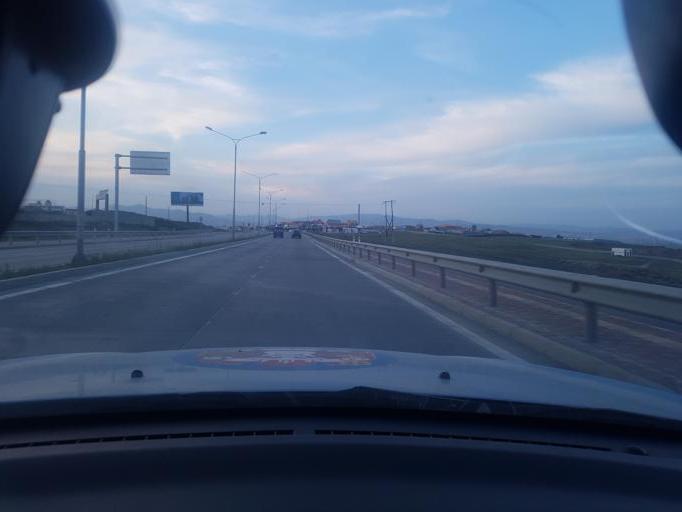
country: MN
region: Ulaanbaatar
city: Ulaanbaatar
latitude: 47.8599
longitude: 106.7880
